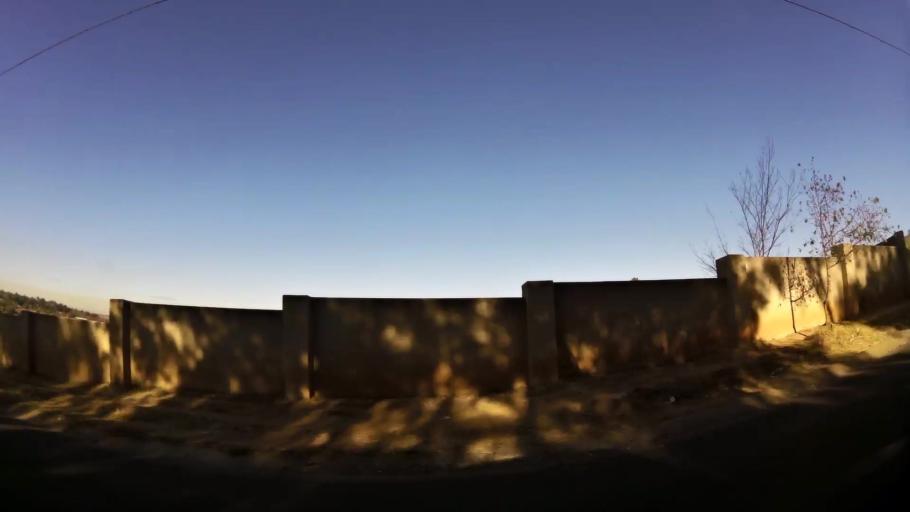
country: ZA
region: Gauteng
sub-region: City of Johannesburg Metropolitan Municipality
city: Midrand
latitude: -26.0170
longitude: 28.1401
